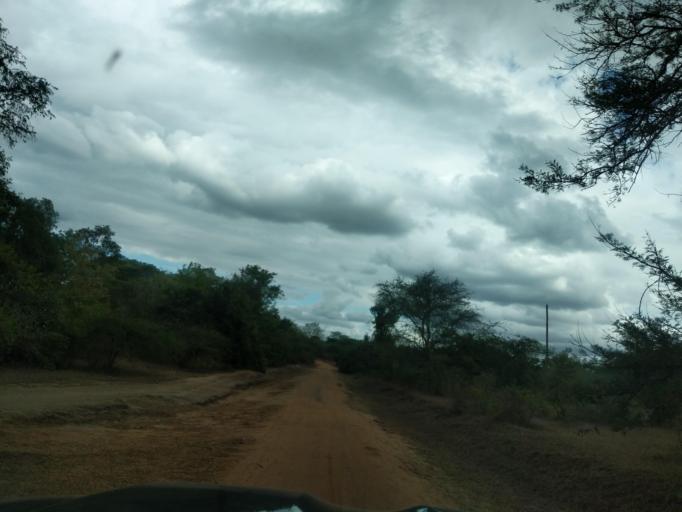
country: TZ
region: Pwani
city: Mvomero
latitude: -5.9382
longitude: 38.4210
